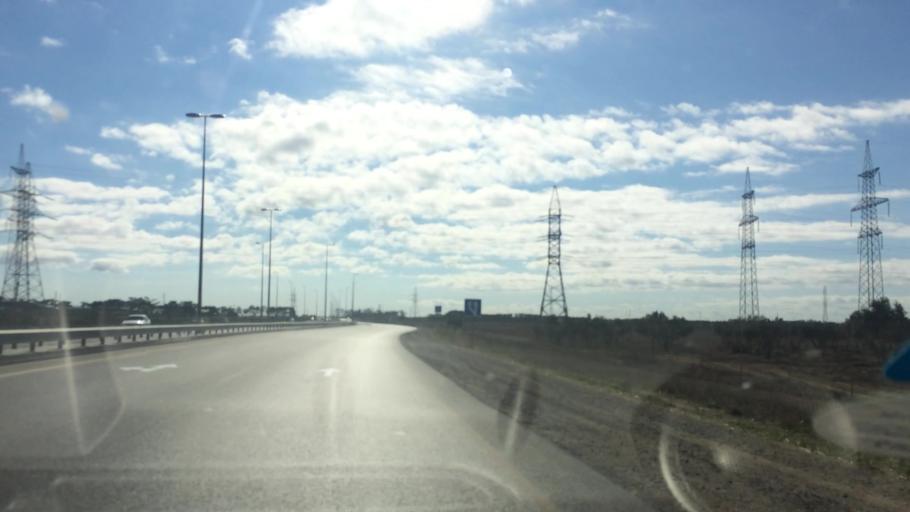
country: AZ
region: Baki
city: Qala
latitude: 40.4380
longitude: 50.1834
